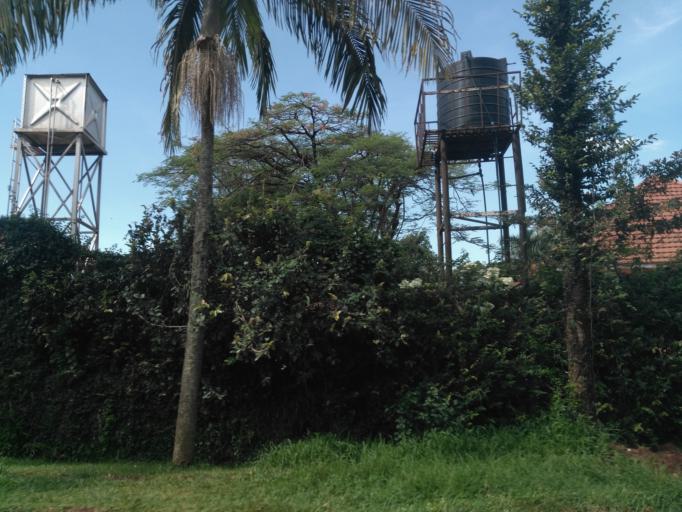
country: UG
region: Central Region
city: Kampala Central Division
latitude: 0.3274
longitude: 32.5779
